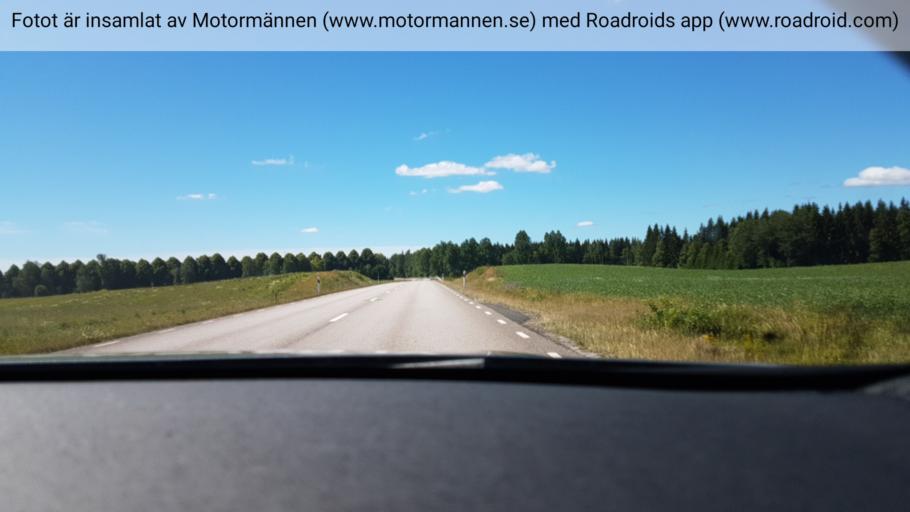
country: SE
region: Vaestra Goetaland
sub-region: Tidaholms Kommun
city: Tidaholm
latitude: 58.0760
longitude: 13.8662
